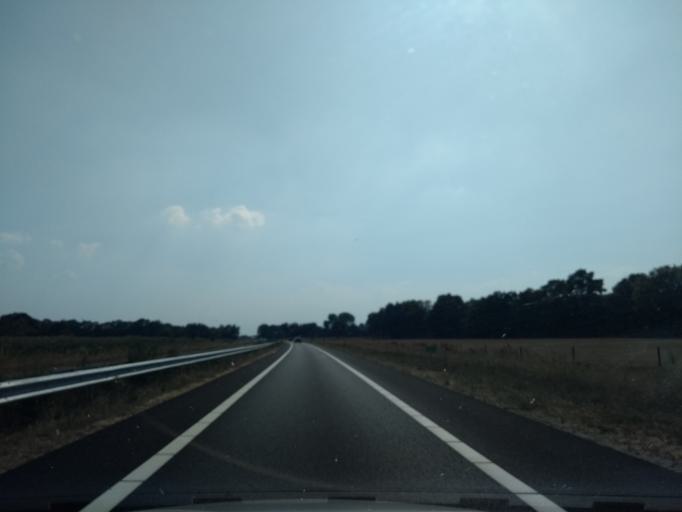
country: NL
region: Overijssel
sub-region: Gemeente Haaksbergen
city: Haaksbergen
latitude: 52.1607
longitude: 6.6952
